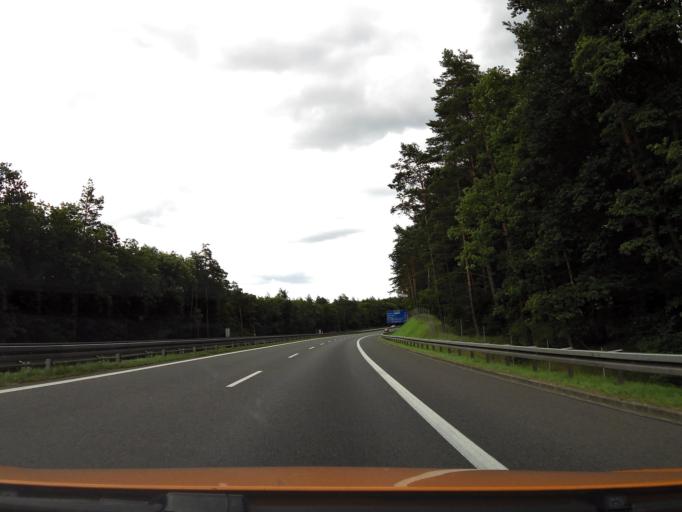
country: PL
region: West Pomeranian Voivodeship
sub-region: Szczecin
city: Szczecin
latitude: 53.3659
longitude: 14.6256
